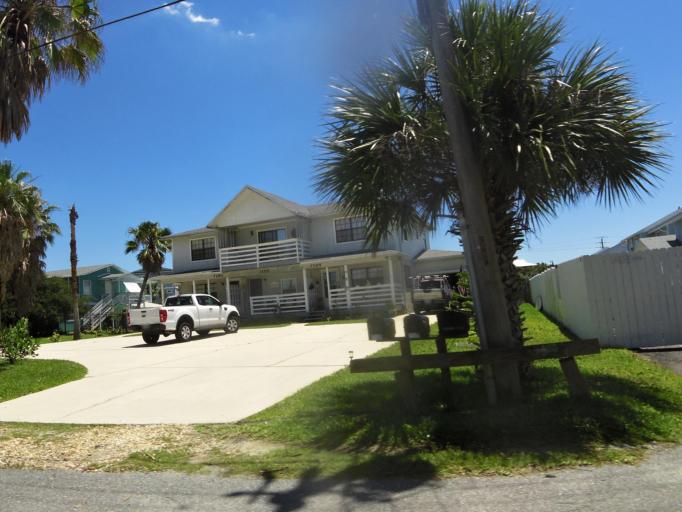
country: US
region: Florida
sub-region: Saint Johns County
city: Butler Beach
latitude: 29.7637
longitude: -81.2530
